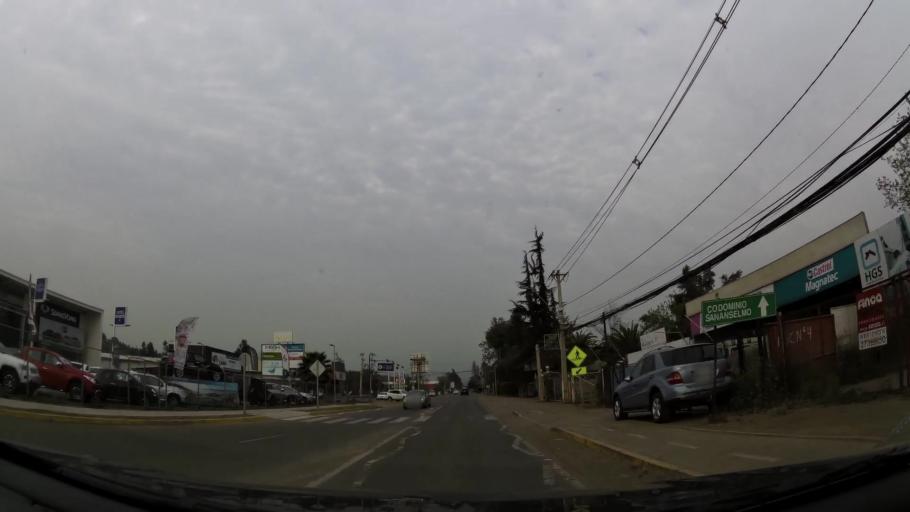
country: CL
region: Santiago Metropolitan
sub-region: Provincia de Chacabuco
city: Chicureo Abajo
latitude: -33.2861
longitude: -70.6762
